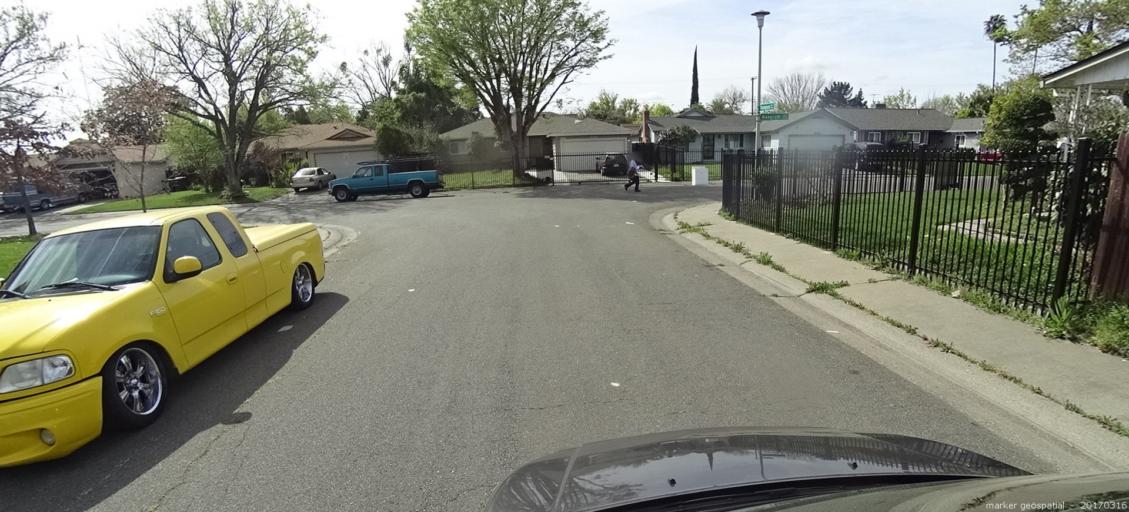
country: US
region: California
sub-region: Sacramento County
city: Parkway
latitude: 38.5075
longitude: -121.4842
